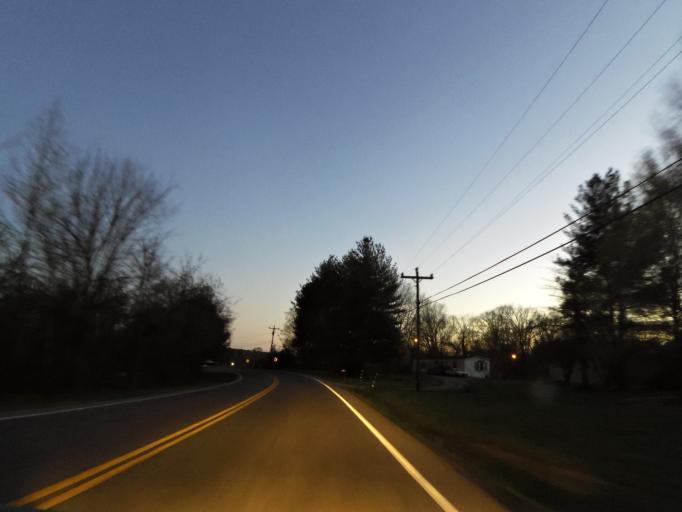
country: US
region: Tennessee
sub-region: Robertson County
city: Coopertown
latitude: 36.3977
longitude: -86.9007
